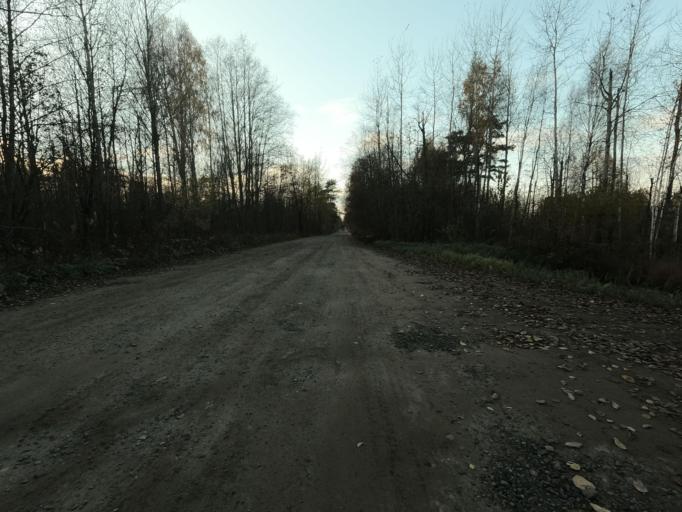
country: RU
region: Leningrad
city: Mga
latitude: 59.7625
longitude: 31.2550
